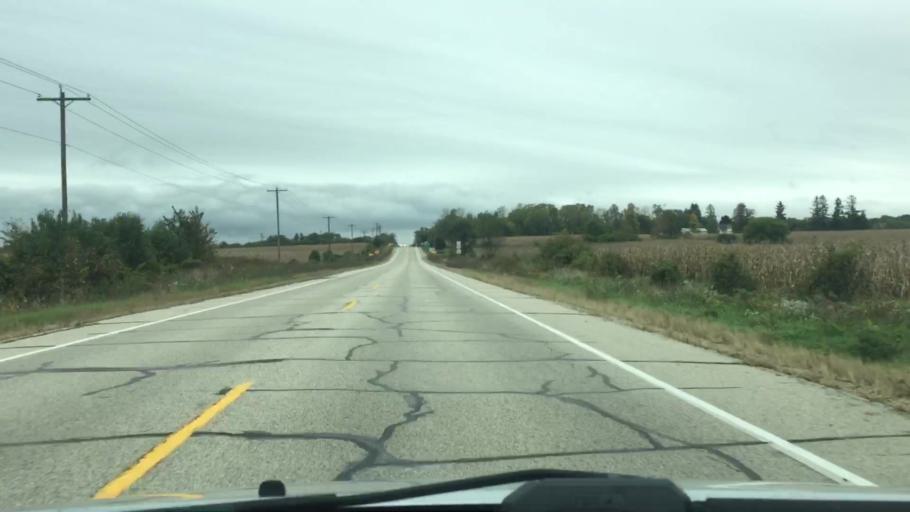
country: US
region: Wisconsin
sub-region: Jefferson County
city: Palmyra
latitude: 42.8049
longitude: -88.5627
